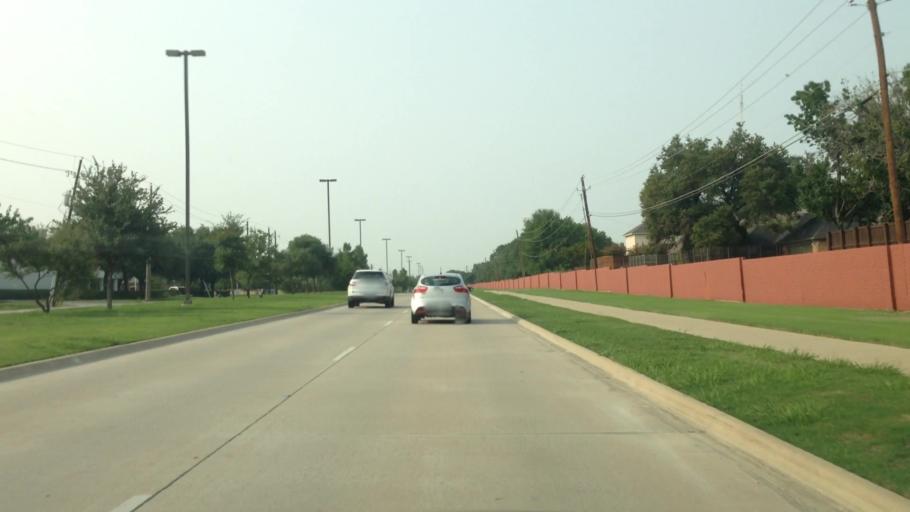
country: US
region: Texas
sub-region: Dallas County
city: Carrollton
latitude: 32.9915
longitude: -96.9201
